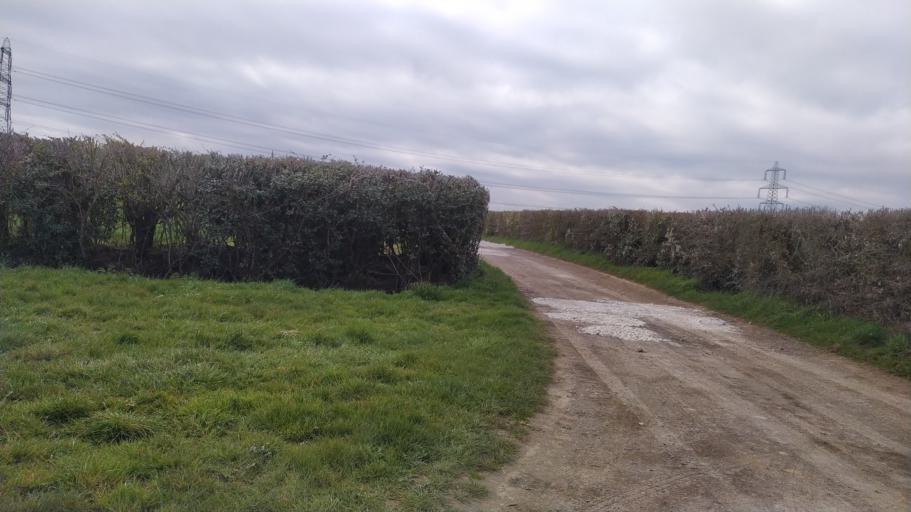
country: GB
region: England
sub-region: West Sussex
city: Petworth
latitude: 51.0176
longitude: -0.5774
